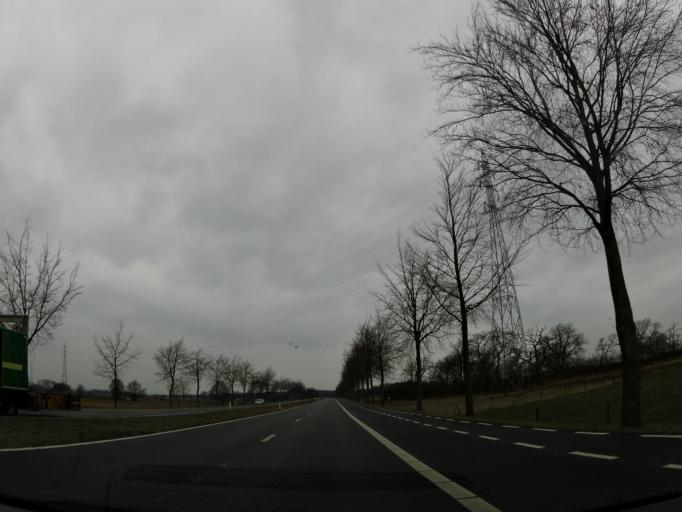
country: BE
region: Flanders
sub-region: Provincie Limburg
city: Maaseik
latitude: 51.0856
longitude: 5.7815
